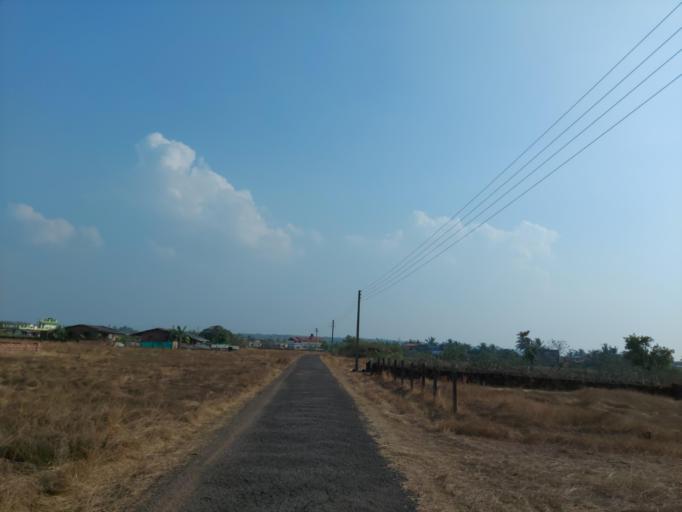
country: IN
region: Maharashtra
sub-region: Ratnagiri
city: Ratnagiri
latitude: 16.9366
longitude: 73.3241
